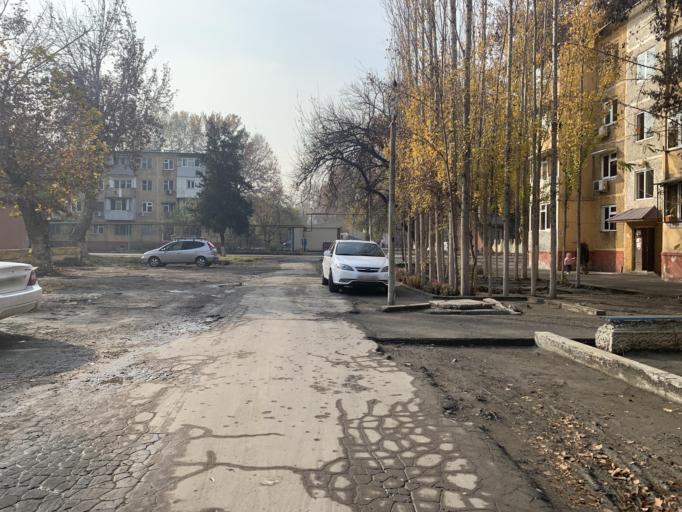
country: UZ
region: Fergana
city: Qo`qon
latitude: 40.5467
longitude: 70.9238
